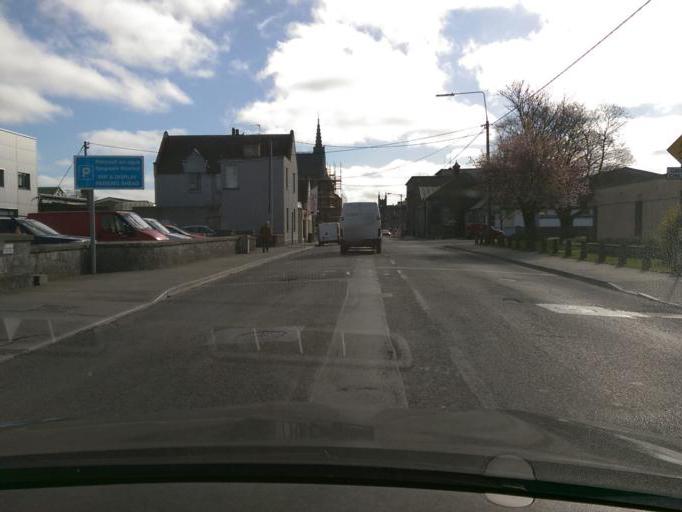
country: IE
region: Connaught
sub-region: County Galway
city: Ballinasloe
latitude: 53.3316
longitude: -8.2284
